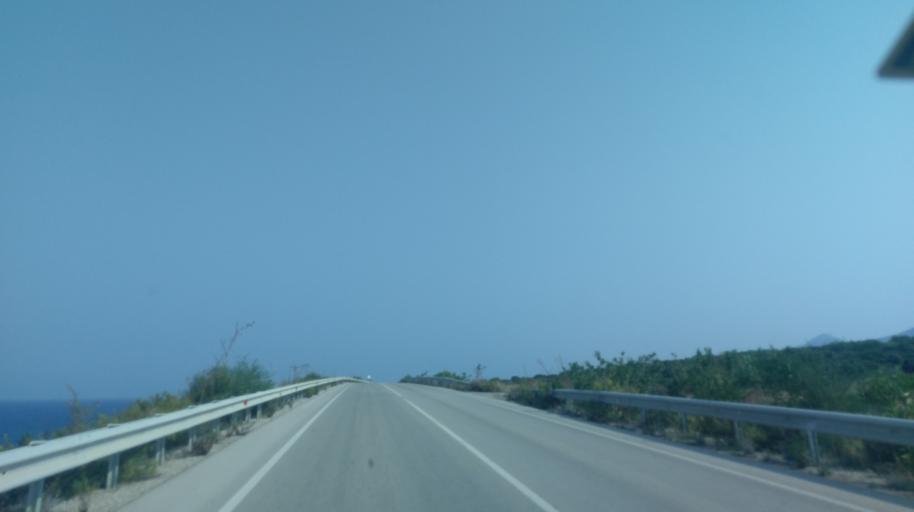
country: CY
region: Ammochostos
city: Trikomo
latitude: 35.4212
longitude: 33.8835
